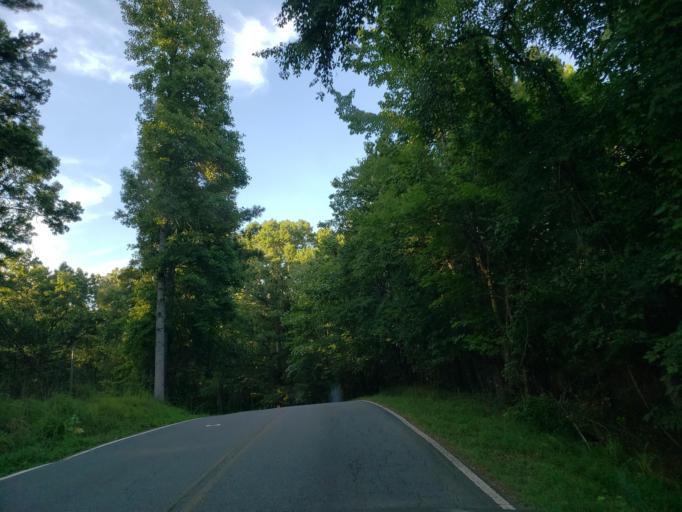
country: US
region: Georgia
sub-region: Bartow County
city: Emerson
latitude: 34.1817
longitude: -84.7069
